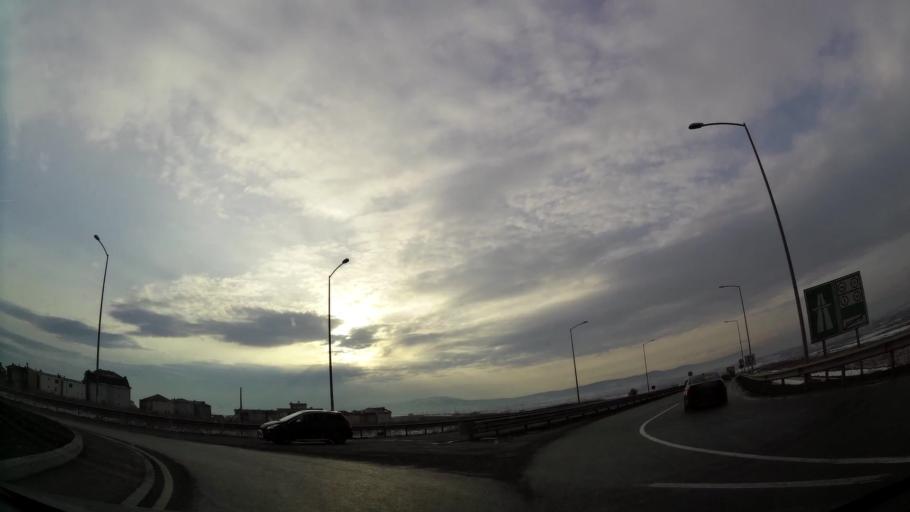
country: XK
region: Pristina
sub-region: Komuna e Prishtines
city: Pristina
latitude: 42.6319
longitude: 21.1444
